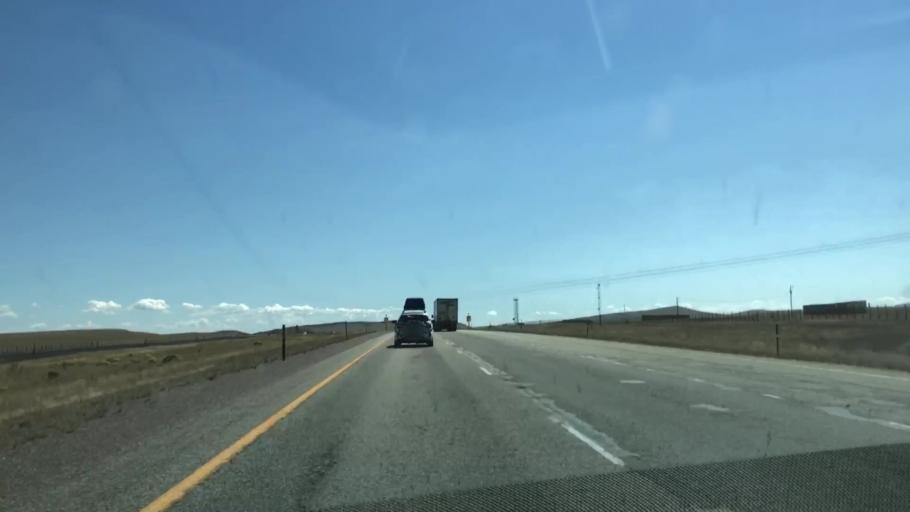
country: US
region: Wyoming
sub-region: Albany County
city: Laramie
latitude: 41.5377
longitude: -106.0782
